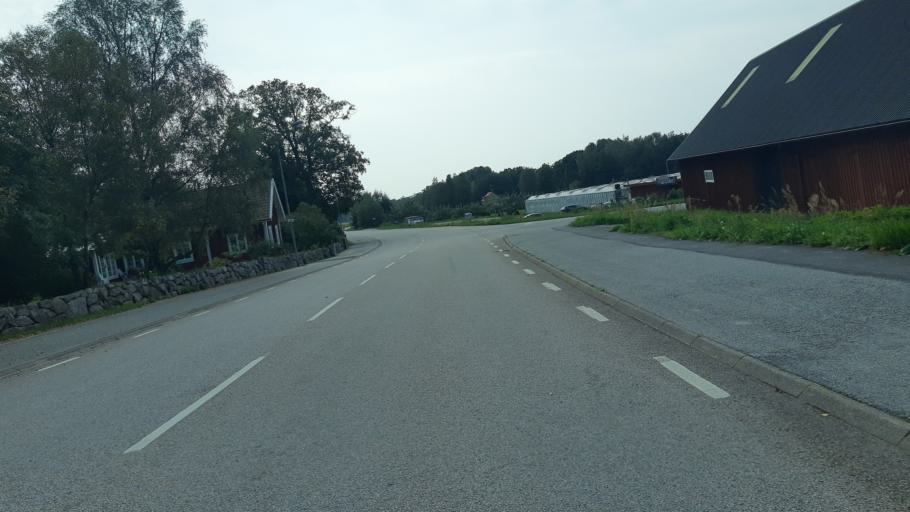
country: SE
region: Blekinge
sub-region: Karlskrona Kommun
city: Nattraby
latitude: 56.2206
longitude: 15.4135
